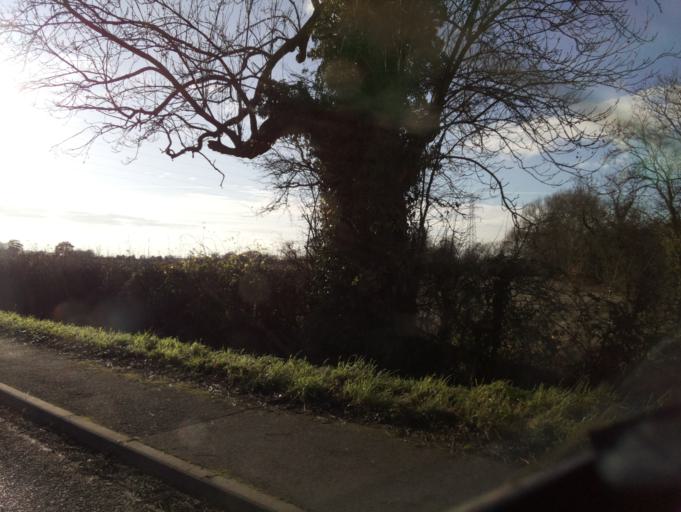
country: GB
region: England
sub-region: Derbyshire
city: Etwall
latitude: 52.8688
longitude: -1.6010
